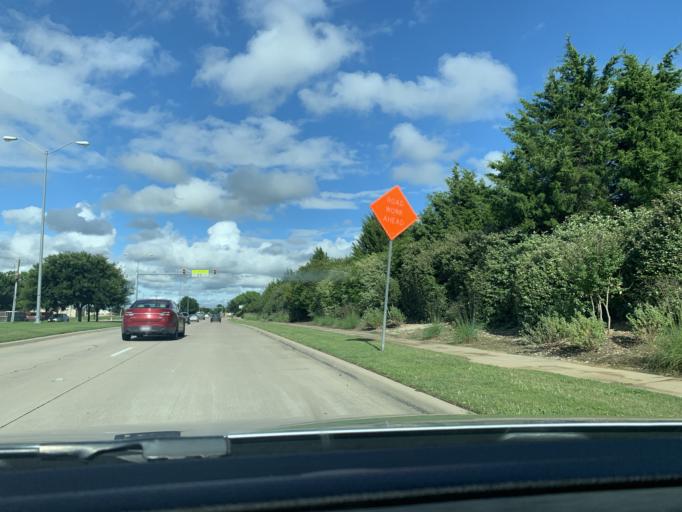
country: US
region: Texas
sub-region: Dallas County
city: Cedar Hill
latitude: 32.6457
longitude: -97.0321
